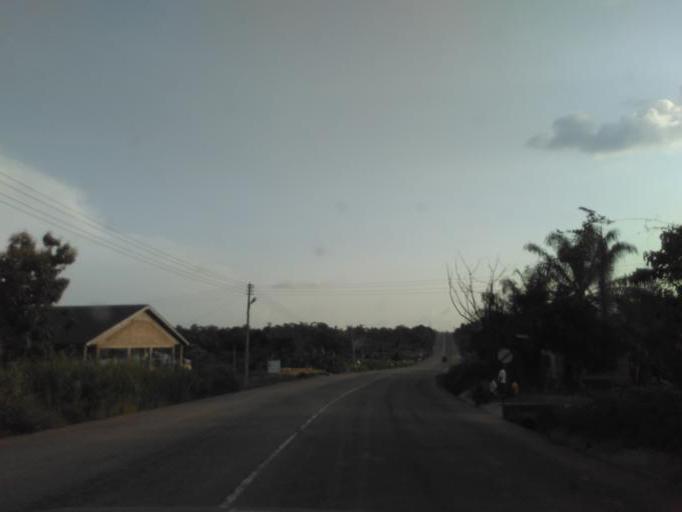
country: GH
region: Ashanti
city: Mamponteng
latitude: 6.6257
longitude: -1.4505
